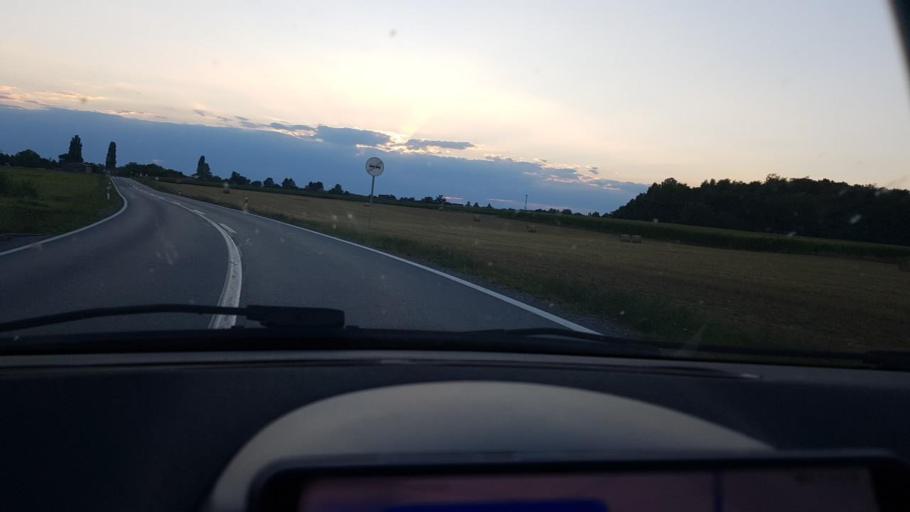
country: HR
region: Bjelovarsko-Bilogorska
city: Zdralovi
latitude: 45.8515
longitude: 16.9391
